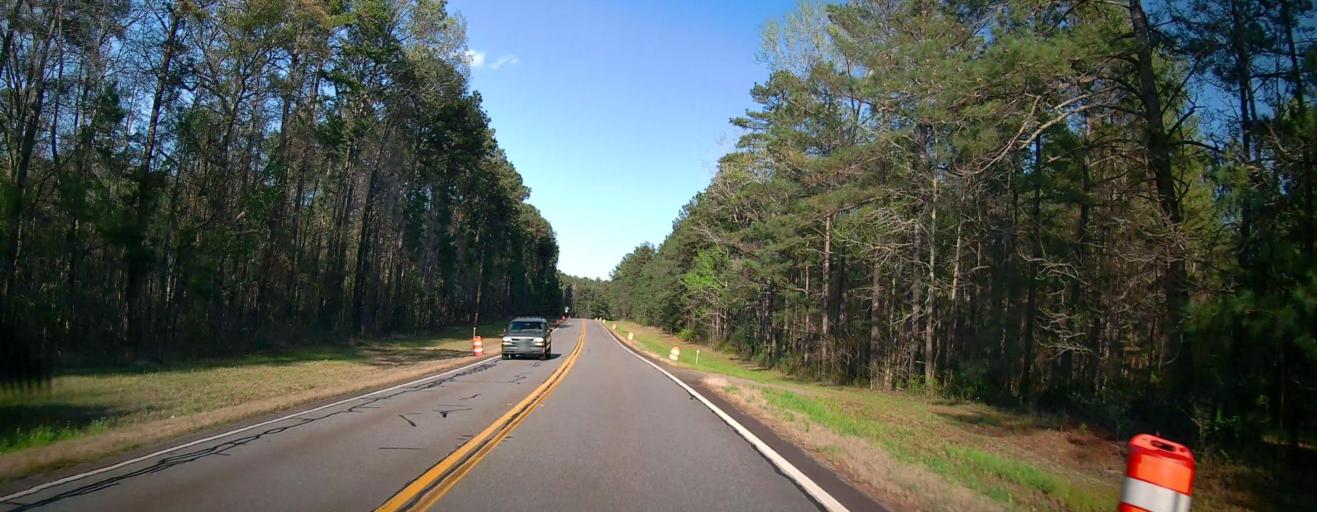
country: US
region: Georgia
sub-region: Baldwin County
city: Milledgeville
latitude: 33.1271
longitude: -83.3121
